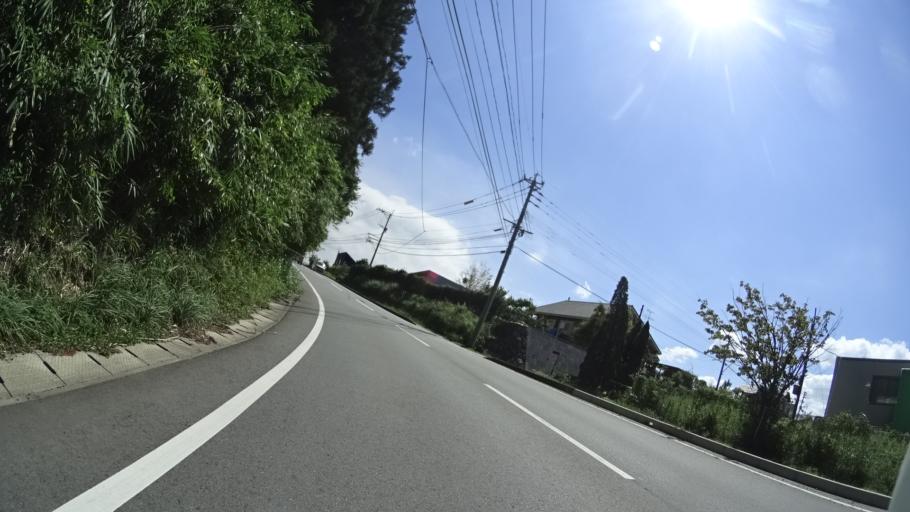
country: JP
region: Kumamoto
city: Aso
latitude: 32.8800
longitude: 131.0035
